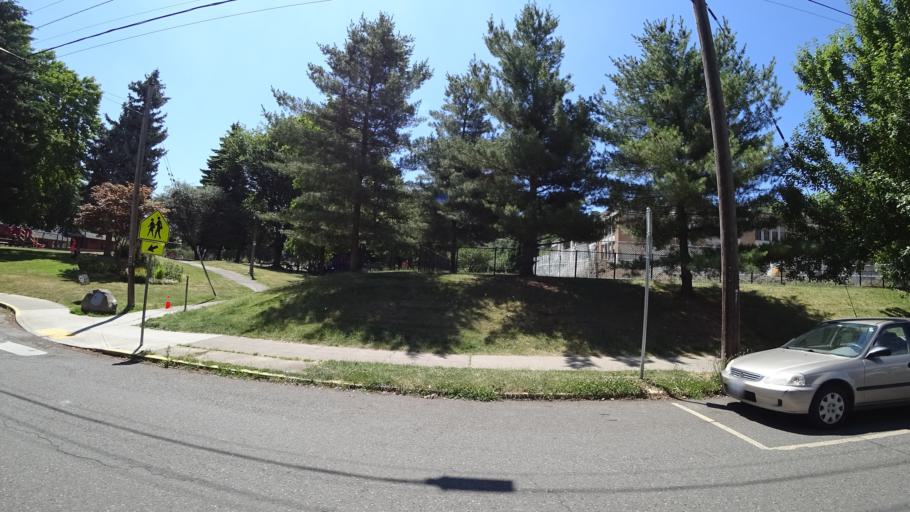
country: US
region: Oregon
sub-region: Multnomah County
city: Portland
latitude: 45.5340
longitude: -122.7050
